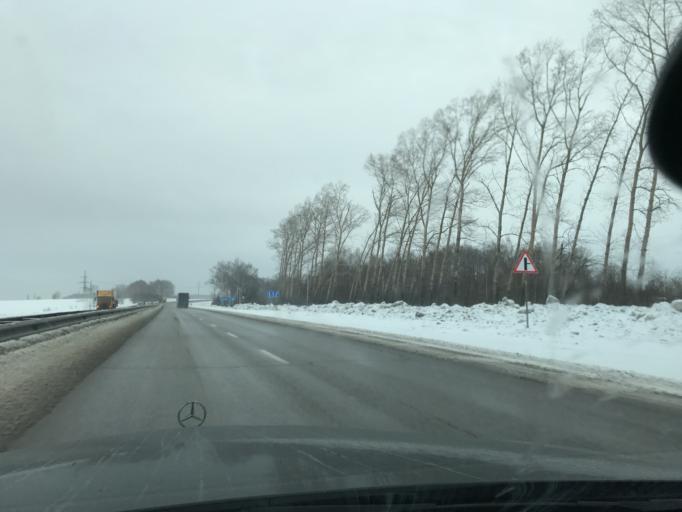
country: RU
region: Vladimir
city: Gorokhovets
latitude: 56.1629
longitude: 42.6108
